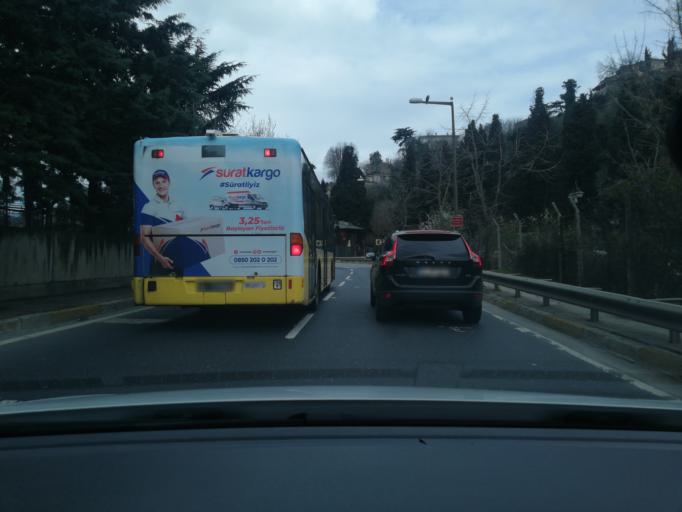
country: TR
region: Istanbul
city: UEskuedar
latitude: 41.0820
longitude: 29.0719
